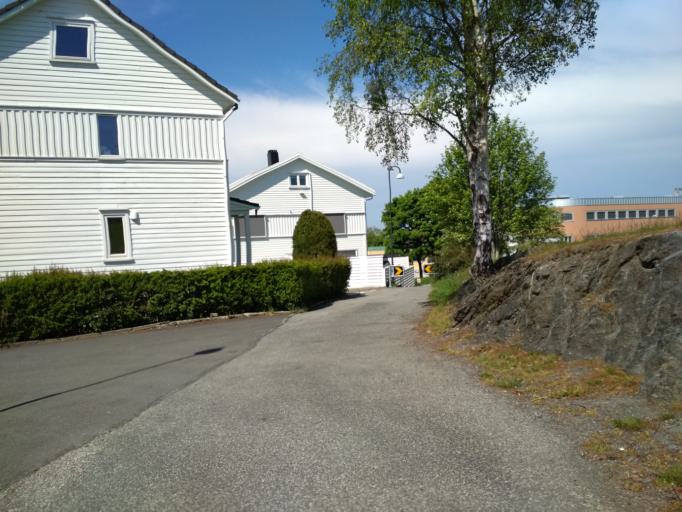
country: NO
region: Rogaland
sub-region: Stavanger
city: Stavanger
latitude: 58.9712
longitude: 5.7180
